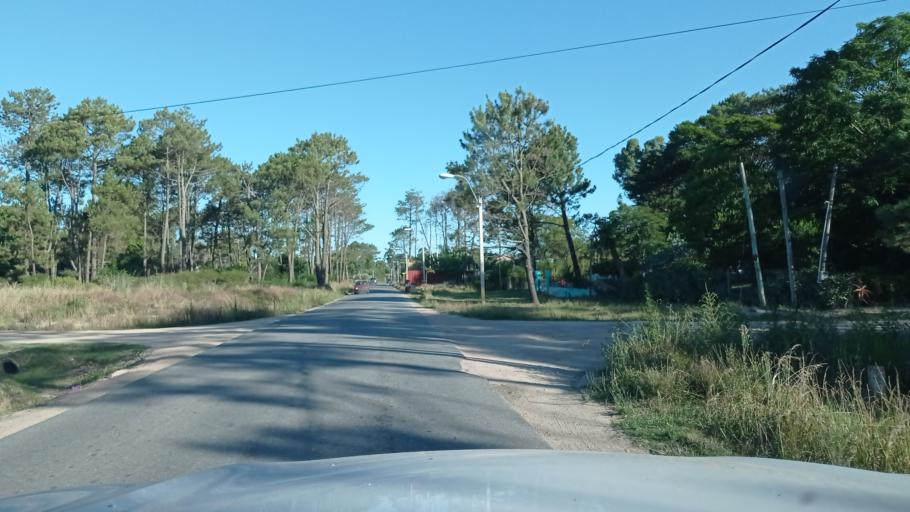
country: UY
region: Canelones
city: Pando
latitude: -34.7975
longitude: -55.9079
